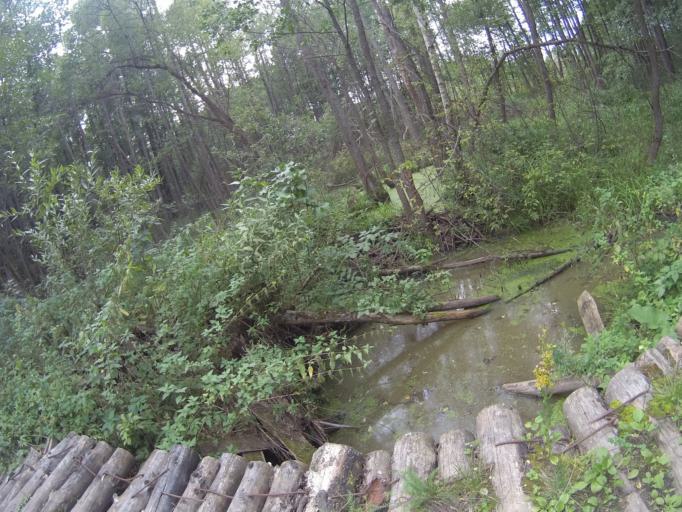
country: RU
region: Vladimir
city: Golovino
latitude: 55.9357
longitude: 40.5125
